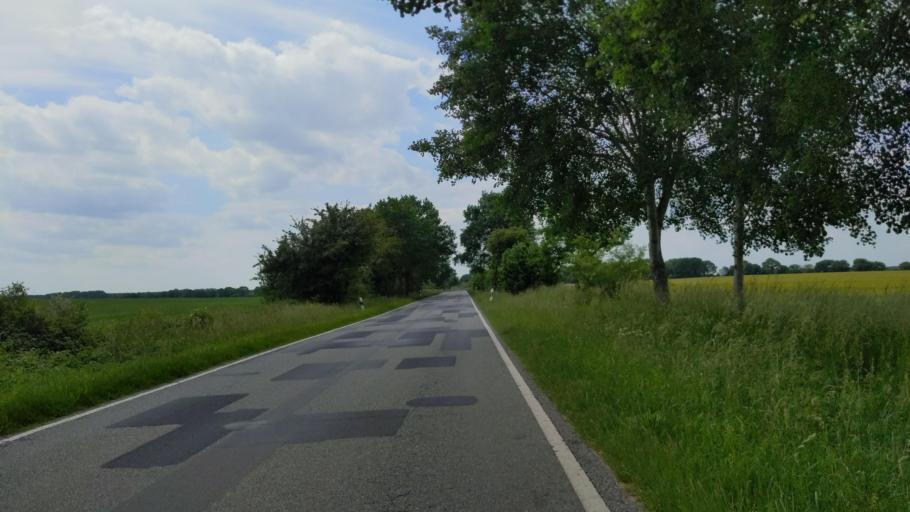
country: DE
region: Mecklenburg-Vorpommern
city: Selmsdorf
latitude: 53.8478
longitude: 10.8052
